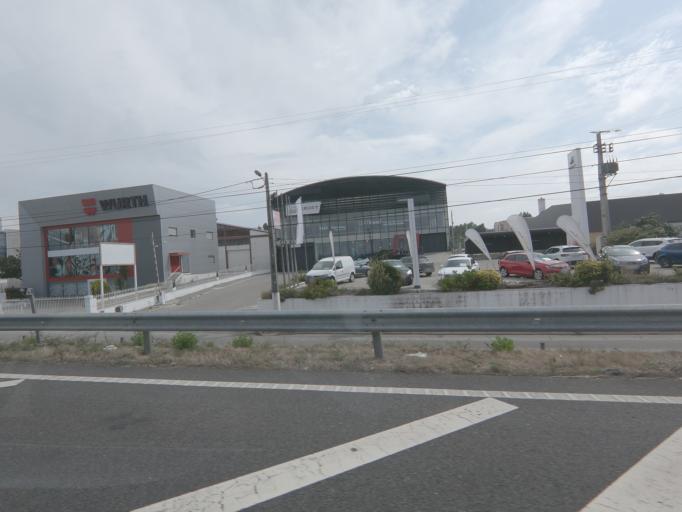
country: PT
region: Leiria
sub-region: Leiria
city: Leiria
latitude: 39.7632
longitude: -8.7871
